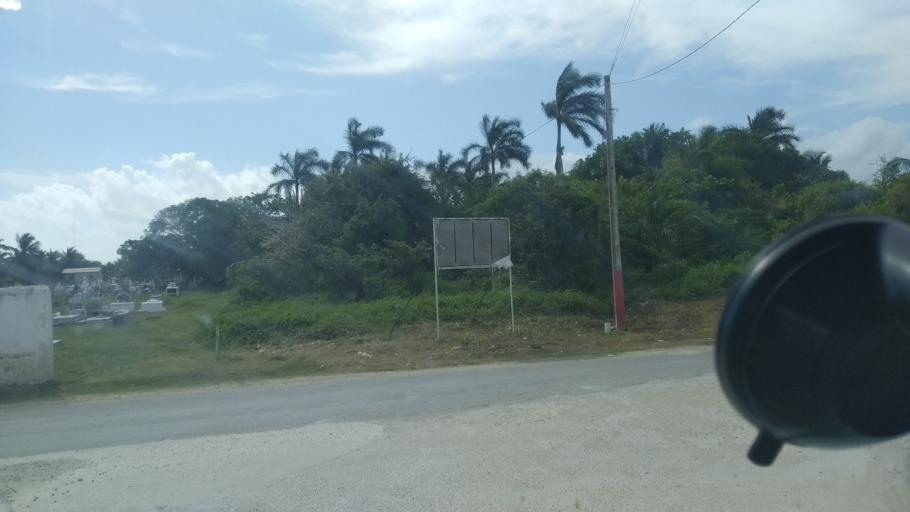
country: BZ
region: Corozal
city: Corozal
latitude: 18.3975
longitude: -88.3805
